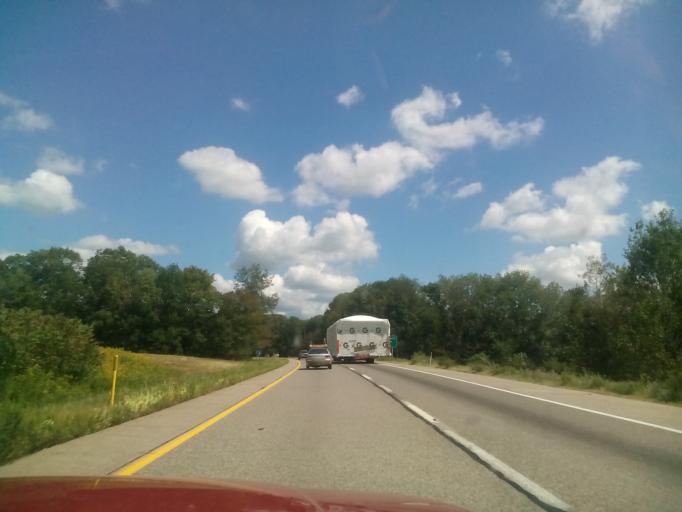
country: US
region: Pennsylvania
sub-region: Luzerne County
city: Conyngham
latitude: 41.0163
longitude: -76.1158
